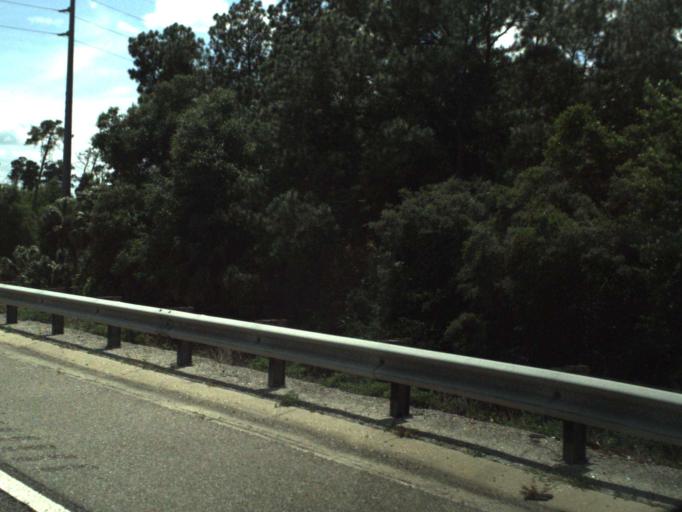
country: US
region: Florida
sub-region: Volusia County
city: Deltona
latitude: 28.9312
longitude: -81.2655
